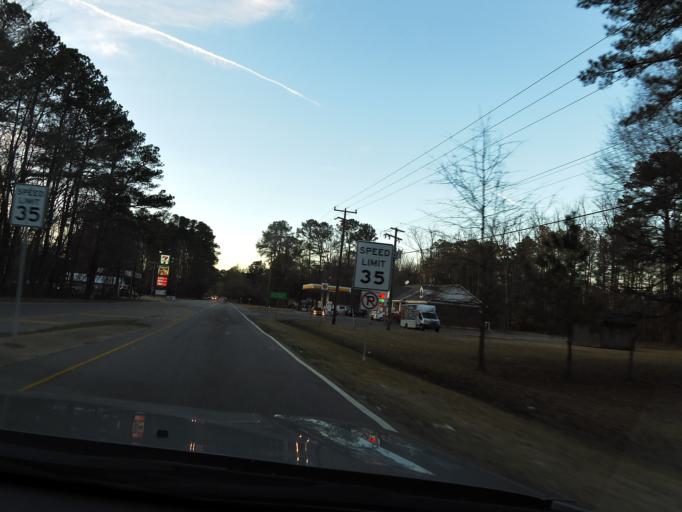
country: US
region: Virginia
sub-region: Southampton County
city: Courtland
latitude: 36.7058
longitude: -77.0514
